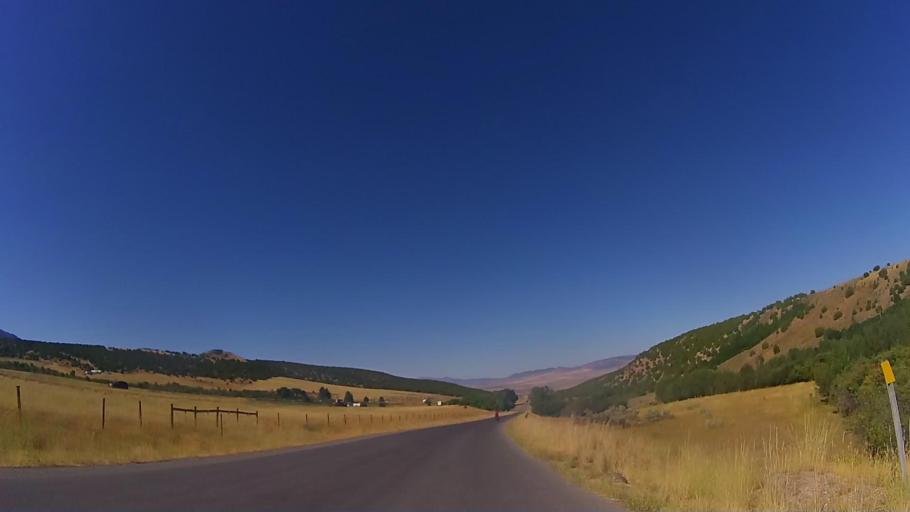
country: US
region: Idaho
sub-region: Oneida County
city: Malad City
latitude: 42.3485
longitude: -112.2255
